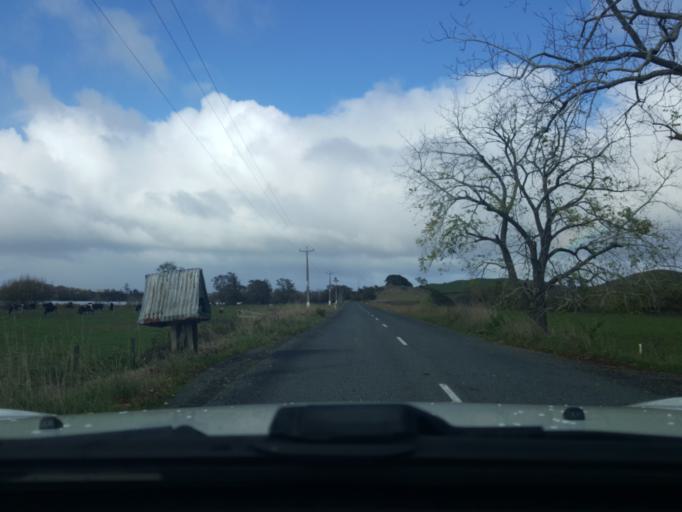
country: NZ
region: Waikato
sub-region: Waikato District
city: Te Kauwhata
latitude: -37.3974
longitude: 175.0582
